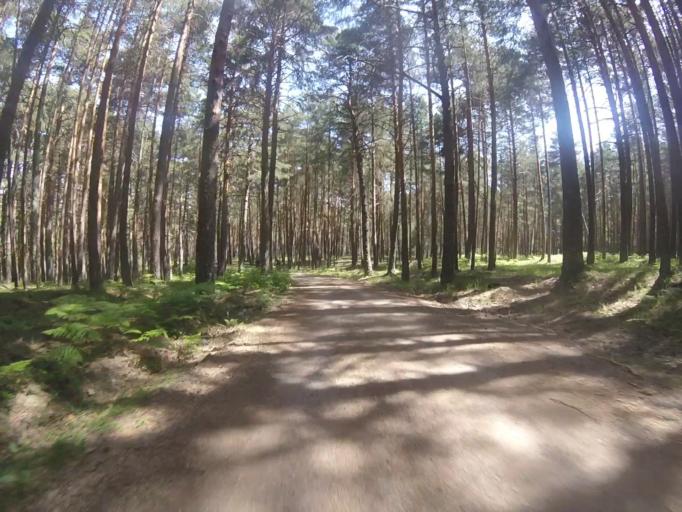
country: ES
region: Madrid
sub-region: Provincia de Madrid
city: Cercedilla
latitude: 40.8140
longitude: -4.0289
